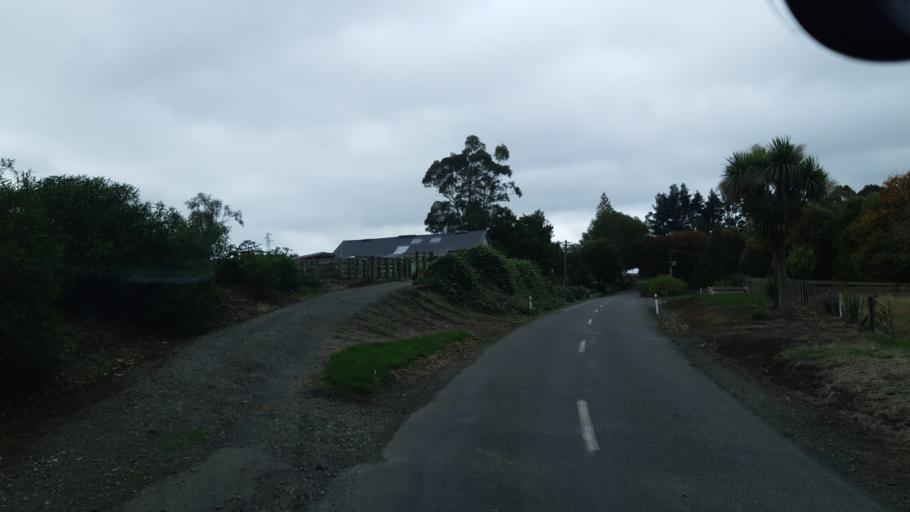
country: NZ
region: Manawatu-Wanganui
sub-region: Ruapehu District
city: Waiouru
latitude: -39.6142
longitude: 175.6438
